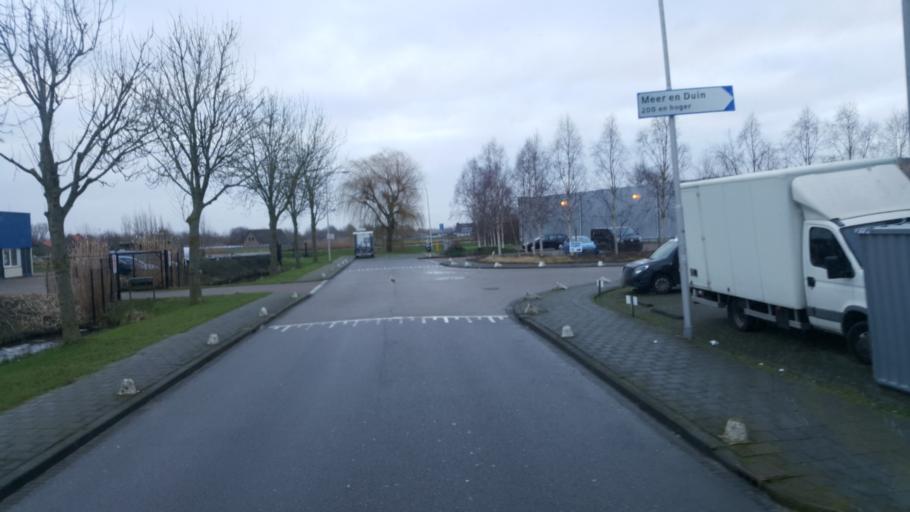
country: NL
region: South Holland
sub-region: Gemeente Lisse
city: Lisse
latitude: 52.2690
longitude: 4.5668
